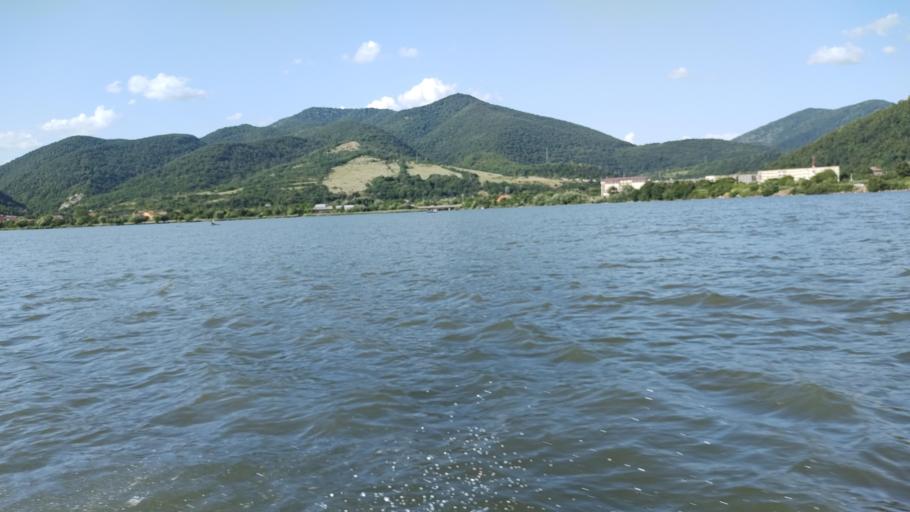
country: RO
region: Caras-Severin
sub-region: Comuna Berzasca
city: Berzasca
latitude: 44.6412
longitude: 21.9448
